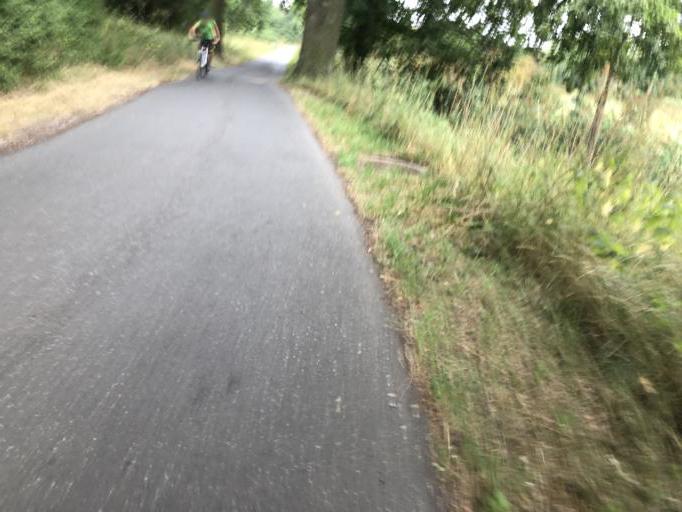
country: DE
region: Bavaria
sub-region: Regierungsbezirk Mittelfranken
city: Furth
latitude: 49.5006
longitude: 10.9782
